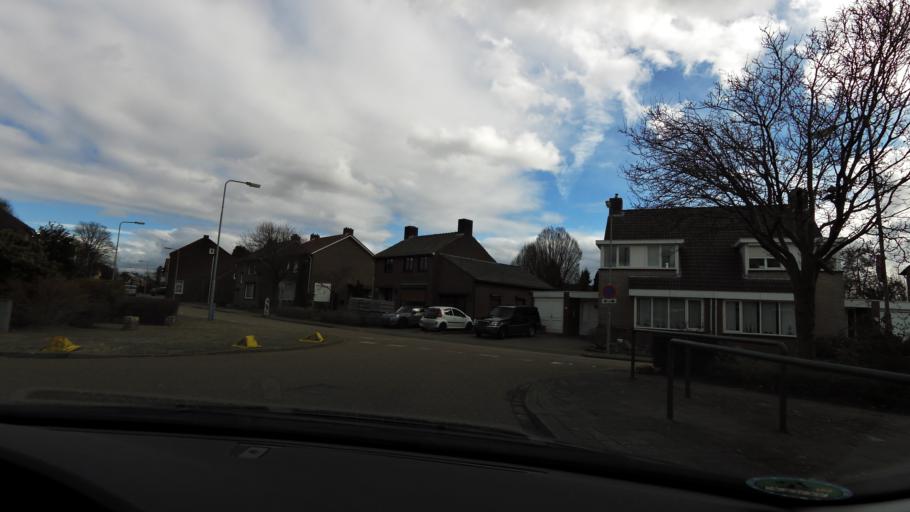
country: NL
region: Limburg
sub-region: Gemeente Nuth
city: Nuth
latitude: 50.9058
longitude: 5.8837
